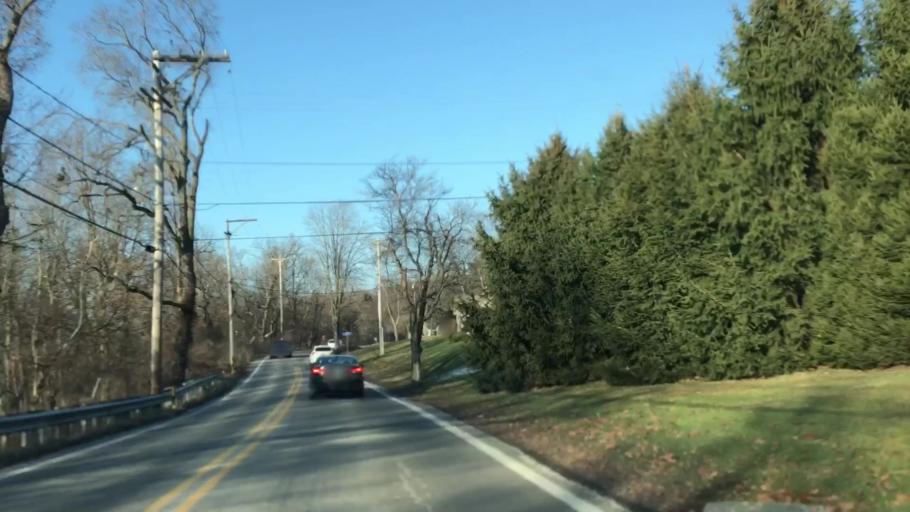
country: US
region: Pennsylvania
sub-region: Allegheny County
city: Gibsonia
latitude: 40.6017
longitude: -79.9772
